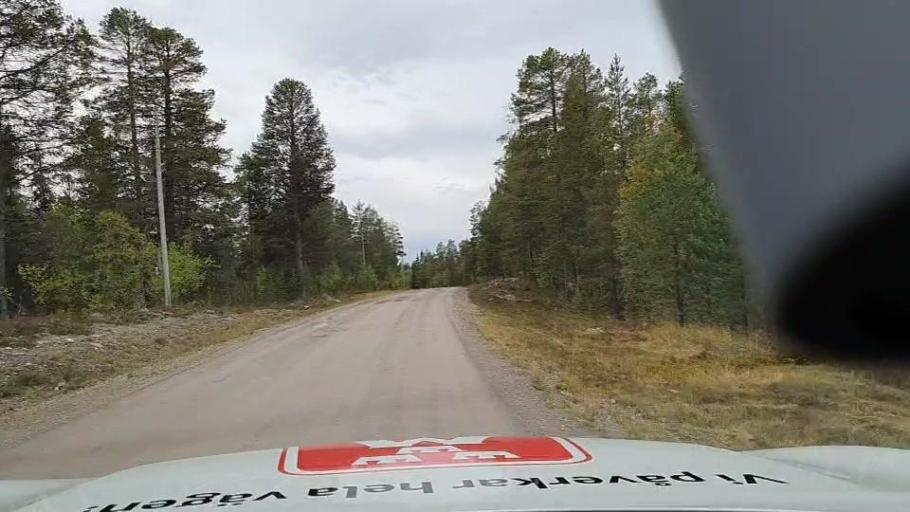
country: NO
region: Hedmark
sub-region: Engerdal
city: Engerdal
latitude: 62.0507
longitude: 12.7229
